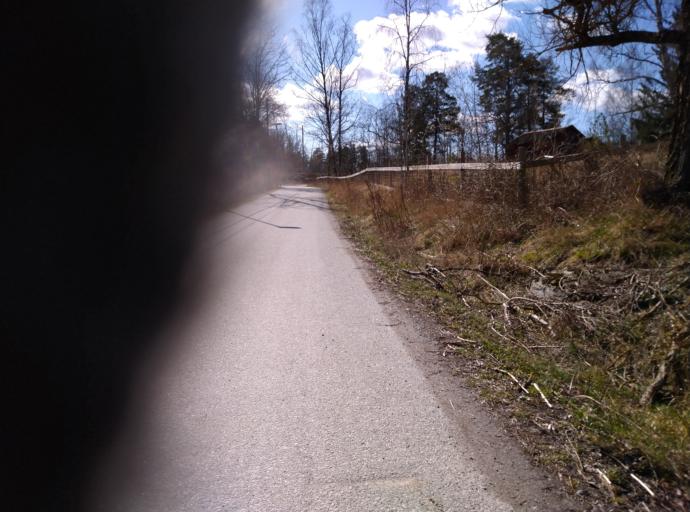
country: SE
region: Stockholm
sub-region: Nacka Kommun
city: Fisksatra
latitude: 59.2950
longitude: 18.2363
